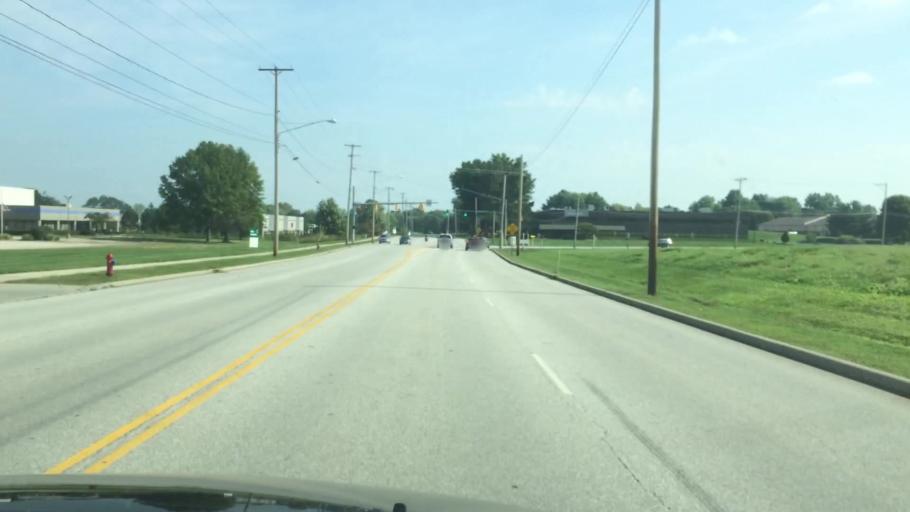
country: US
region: Ohio
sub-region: Summit County
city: Silver Lake
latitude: 41.1913
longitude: -81.4628
